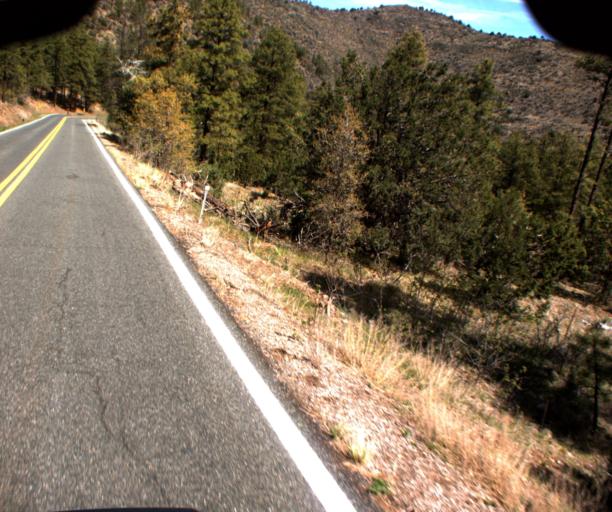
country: US
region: Arizona
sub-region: Yavapai County
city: Clarkdale
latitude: 34.7183
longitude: -112.1545
